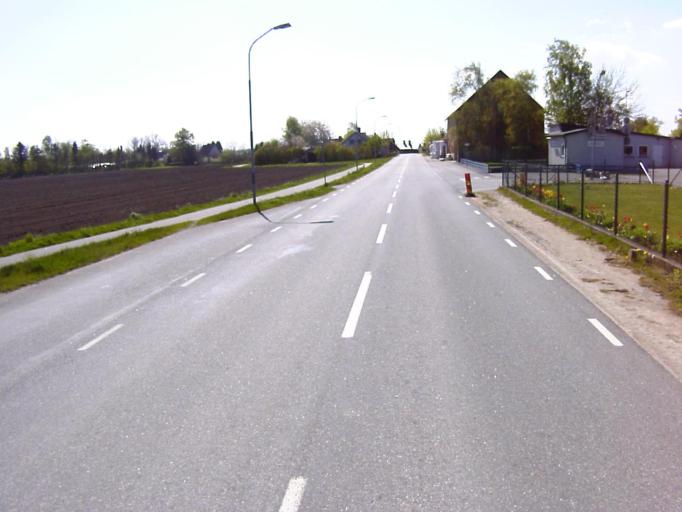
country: SE
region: Skane
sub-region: Kristianstads Kommun
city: Fjalkinge
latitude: 56.0129
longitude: 14.2341
